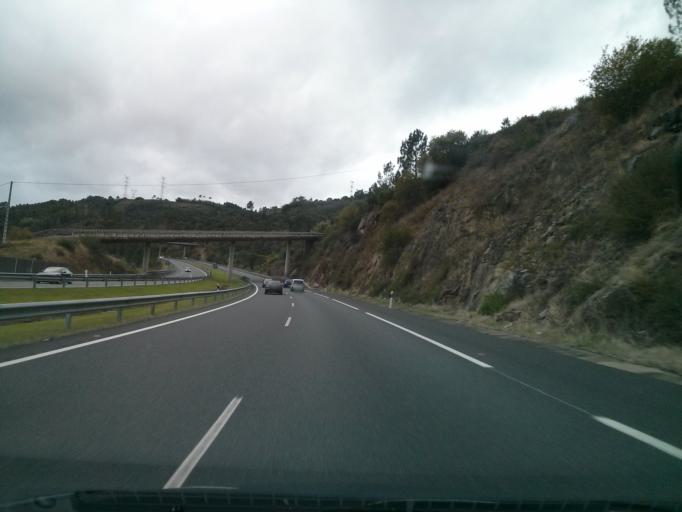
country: ES
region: Galicia
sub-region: Provincia de Ourense
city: Cenlle
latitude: 42.3342
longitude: -8.0698
